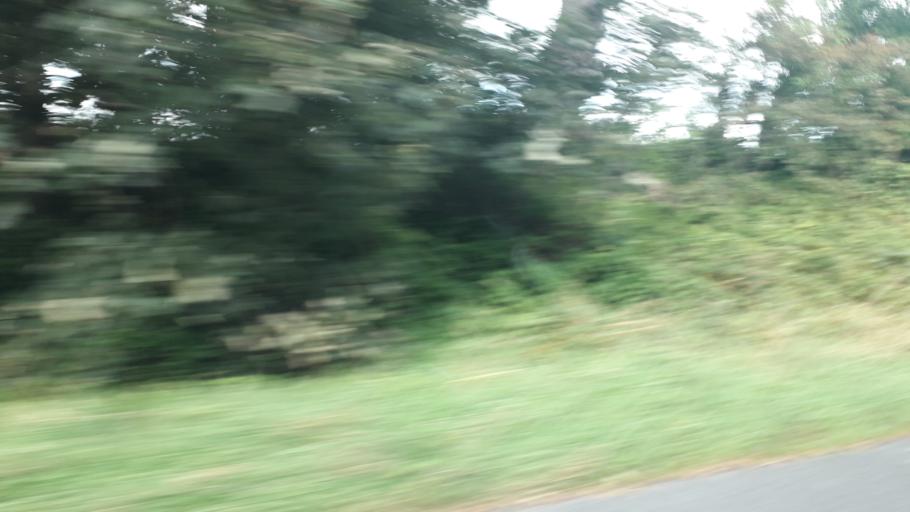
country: IE
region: Leinster
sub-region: Lu
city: Dundalk
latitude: 54.0346
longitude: -6.3791
